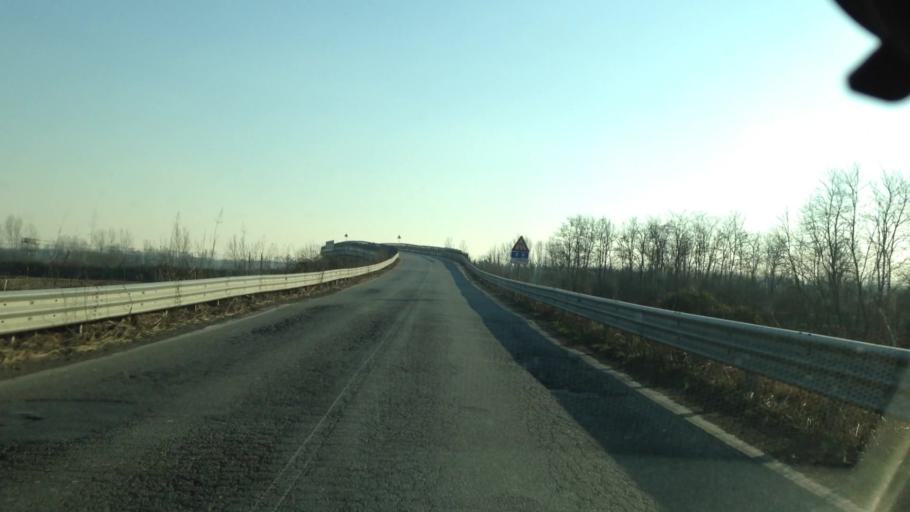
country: IT
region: Piedmont
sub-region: Provincia di Alessandria
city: Felizzano
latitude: 44.8997
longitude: 8.4495
